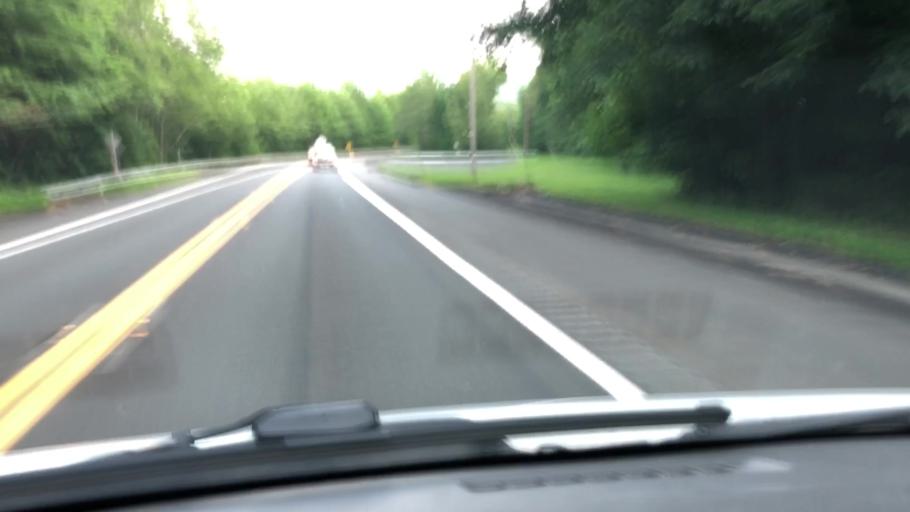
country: US
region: Massachusetts
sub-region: Hampshire County
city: Chesterfield
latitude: 42.4494
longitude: -72.8191
